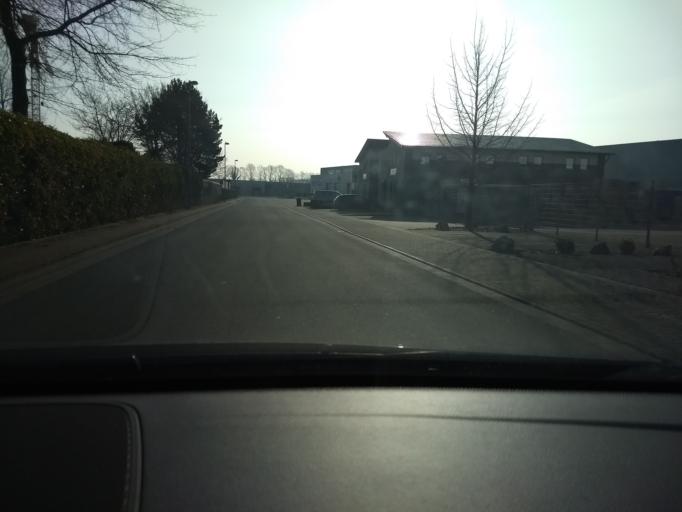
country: DE
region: North Rhine-Westphalia
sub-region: Regierungsbezirk Munster
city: Rhede
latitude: 51.8305
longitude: 6.7173
